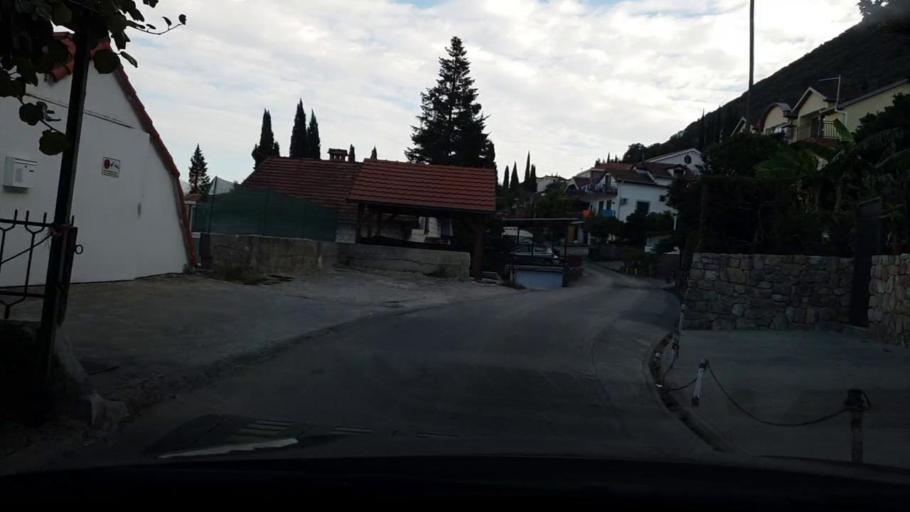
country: ME
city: Igalo
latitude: 42.4374
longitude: 18.5119
